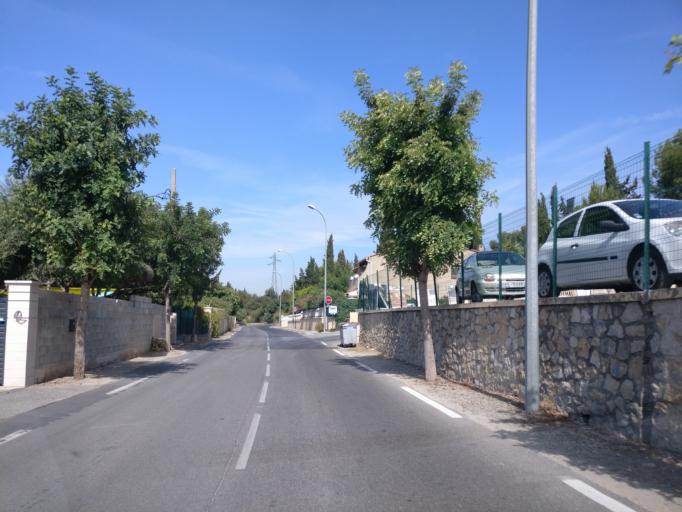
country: FR
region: Provence-Alpes-Cote d'Azur
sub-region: Departement du Var
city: Sanary-sur-Mer
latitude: 43.1302
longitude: 5.8167
